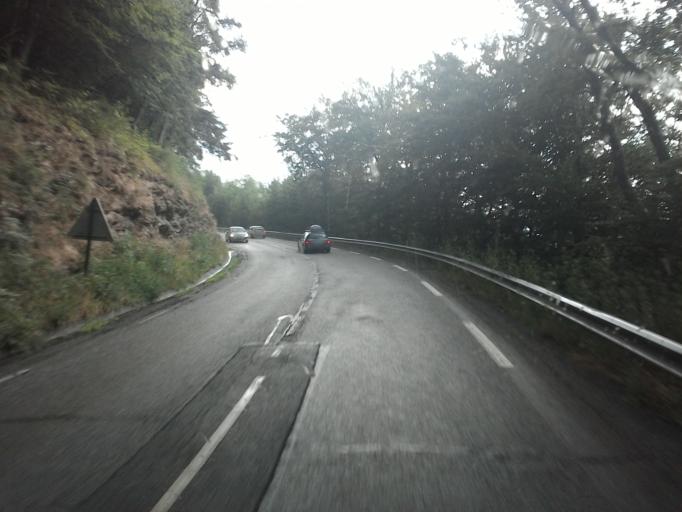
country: FR
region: Rhone-Alpes
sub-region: Departement de l'Isere
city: La Mure
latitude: 44.8337
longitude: 5.9135
